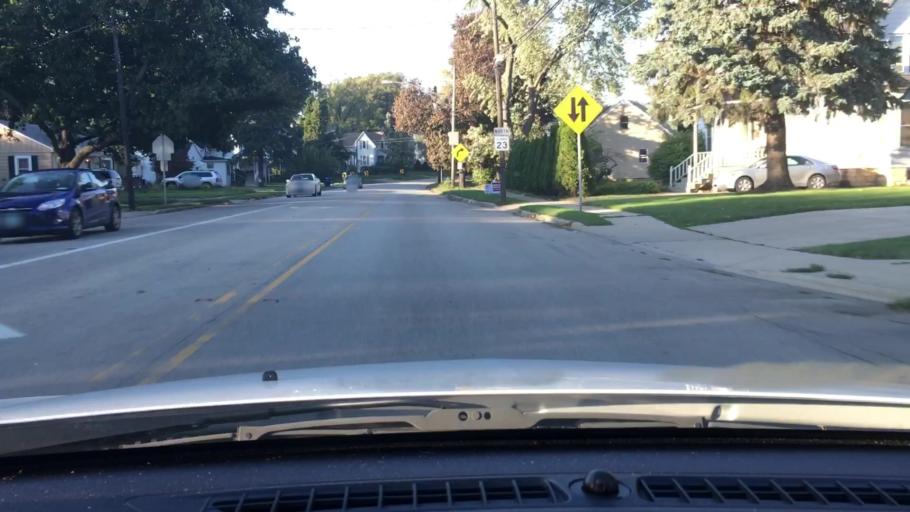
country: US
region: Illinois
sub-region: DeKalb County
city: DeKalb
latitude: 41.9220
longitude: -88.7534
